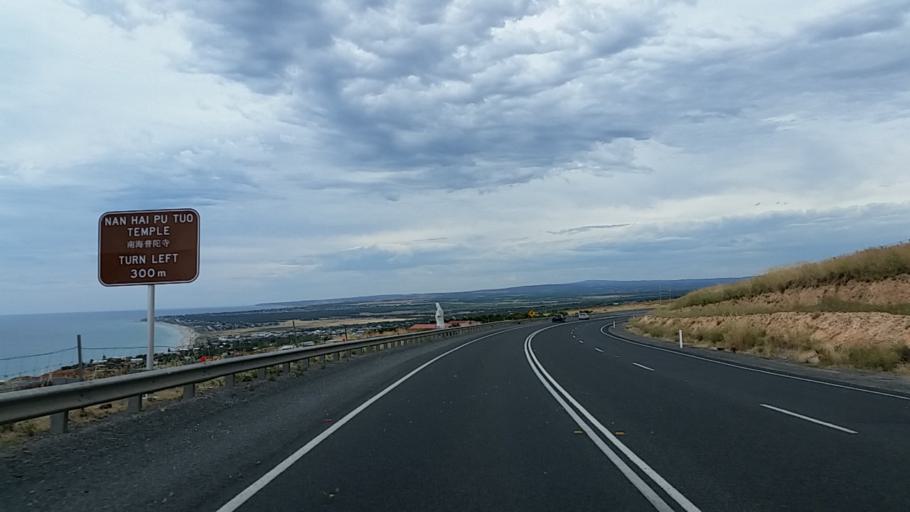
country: AU
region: South Australia
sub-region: Onkaparinga
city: Port Willunga
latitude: -35.3534
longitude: 138.4477
